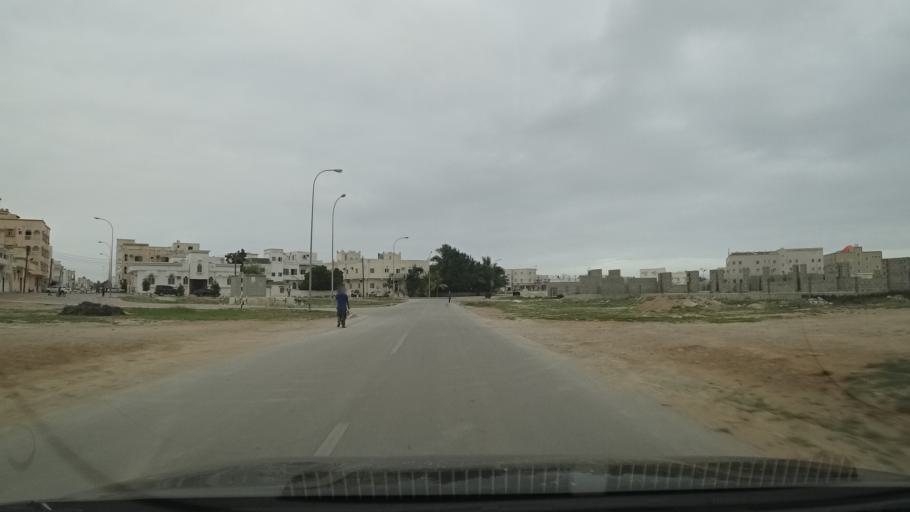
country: OM
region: Zufar
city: Salalah
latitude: 17.0237
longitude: 54.1547
